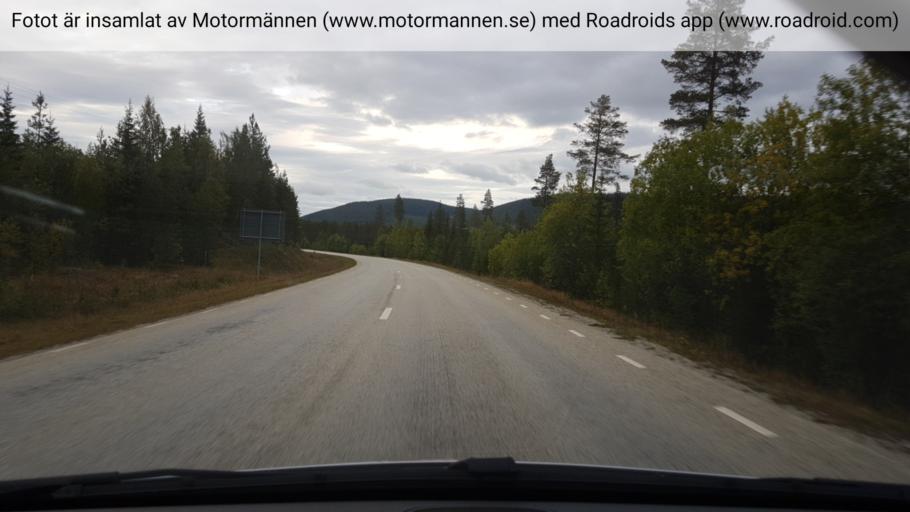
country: SE
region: Jaemtland
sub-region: Bergs Kommun
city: Hoverberg
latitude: 62.4823
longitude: 14.2305
